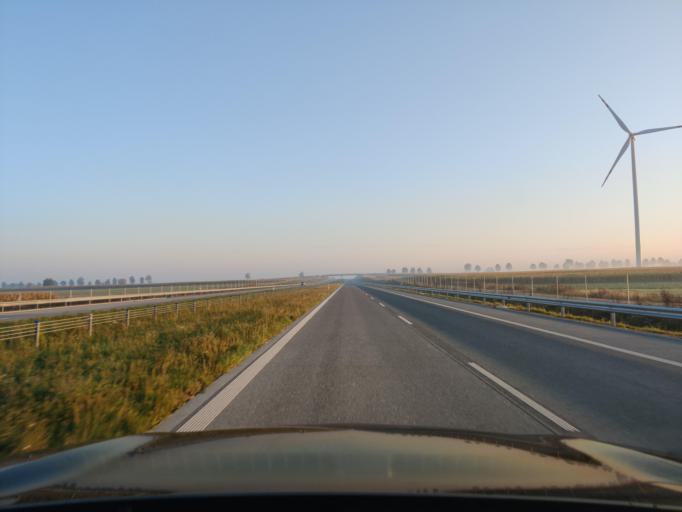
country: PL
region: Masovian Voivodeship
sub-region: Powiat mlawski
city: Wisniewo
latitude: 53.0537
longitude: 20.3628
